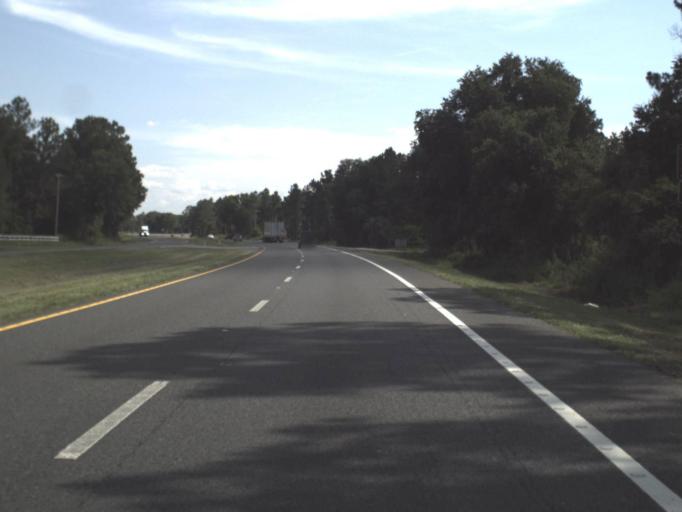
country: US
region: Florida
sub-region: Marion County
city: Citra
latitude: 29.4759
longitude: -82.1047
